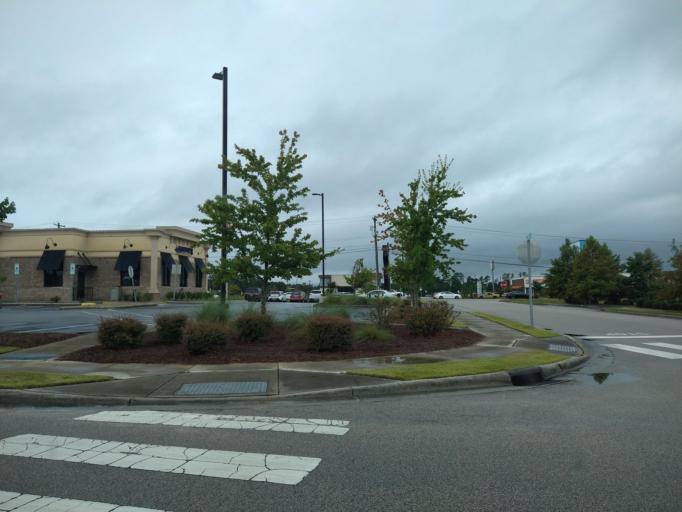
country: US
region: North Carolina
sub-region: Onslow County
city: Pumpkin Center
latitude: 34.7983
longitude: -77.4118
